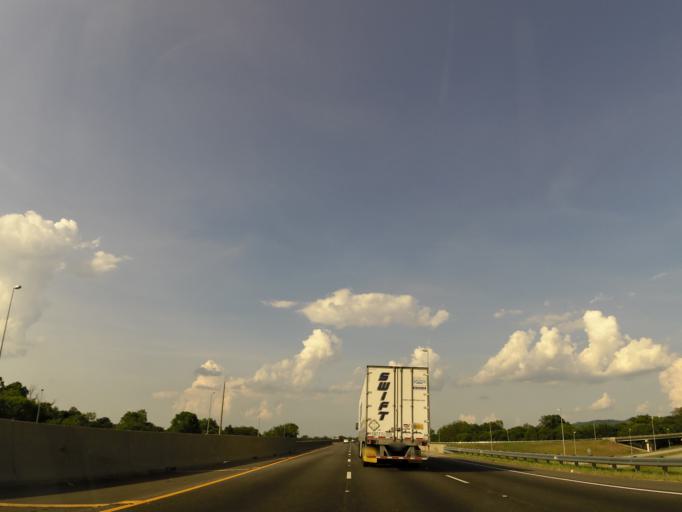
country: US
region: Alabama
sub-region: Jefferson County
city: Tarrant
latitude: 33.5469
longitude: -86.7500
